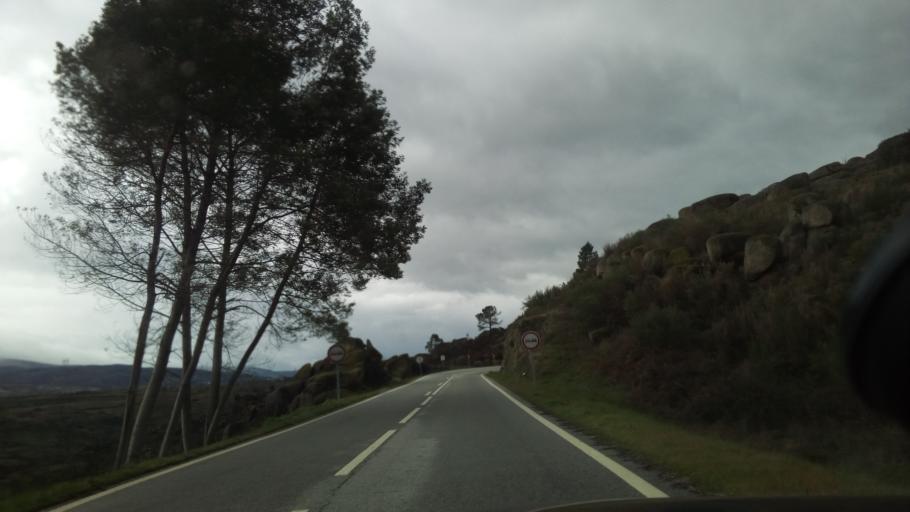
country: PT
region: Guarda
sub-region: Fornos de Algodres
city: Fornos de Algodres
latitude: 40.5584
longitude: -7.5624
